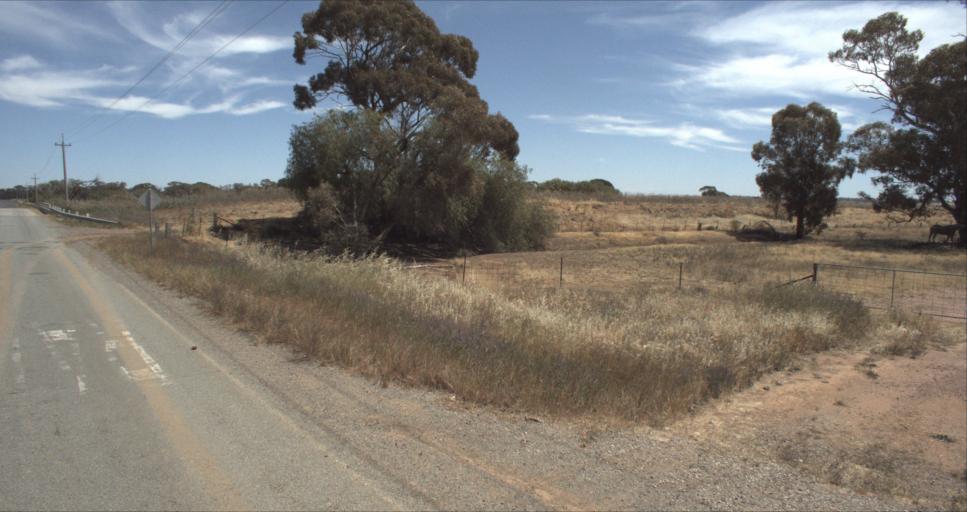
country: AU
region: New South Wales
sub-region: Leeton
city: Leeton
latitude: -34.6484
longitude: 146.4702
